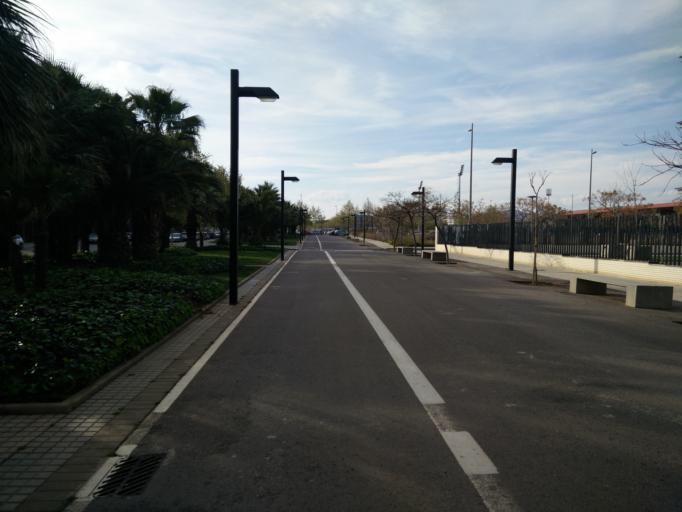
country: ES
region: Valencia
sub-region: Provincia de Castello
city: Castello de la Plana
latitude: 39.9789
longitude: -0.0587
